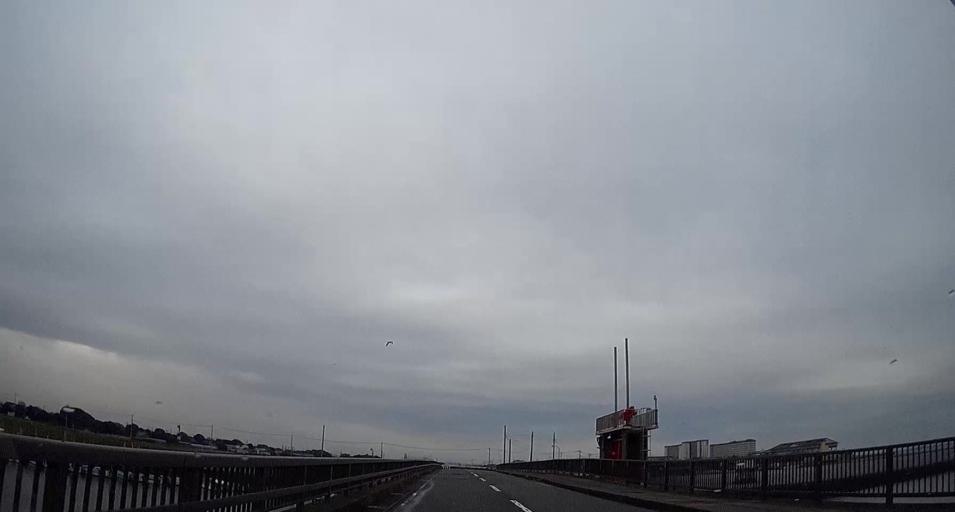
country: JP
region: Chiba
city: Kisarazu
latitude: 35.4281
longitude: 139.9031
